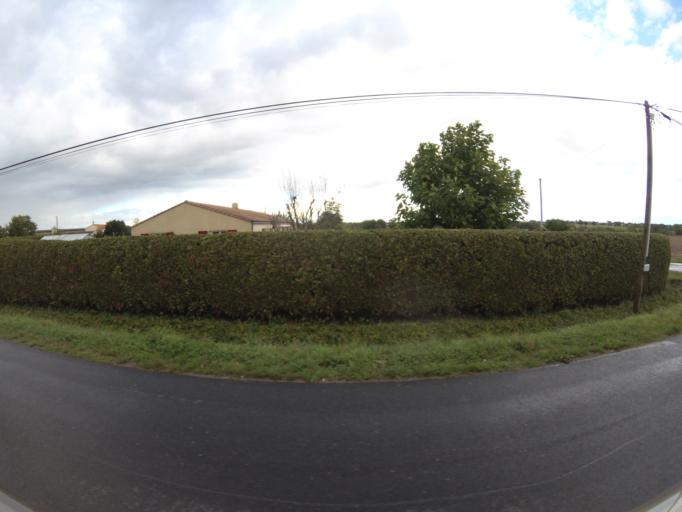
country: FR
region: Pays de la Loire
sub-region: Departement de la Loire-Atlantique
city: Saint-Lumine-de-Clisson
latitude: 47.0709
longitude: -1.3244
